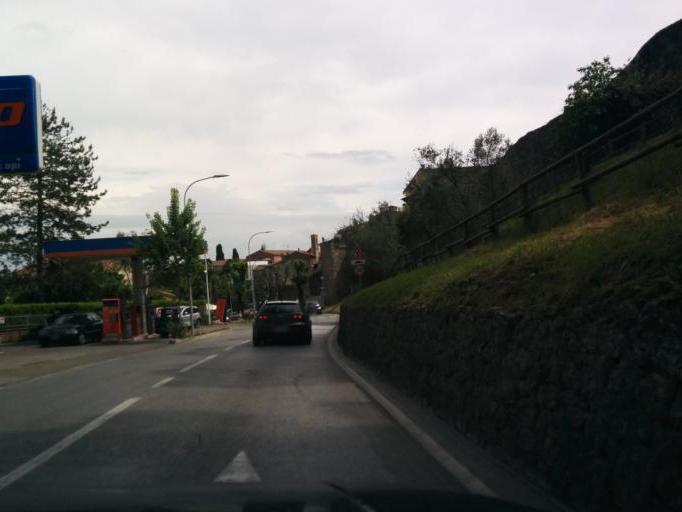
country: IT
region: Tuscany
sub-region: Provincia di Siena
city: San Gimignano
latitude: 43.4685
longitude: 11.0402
